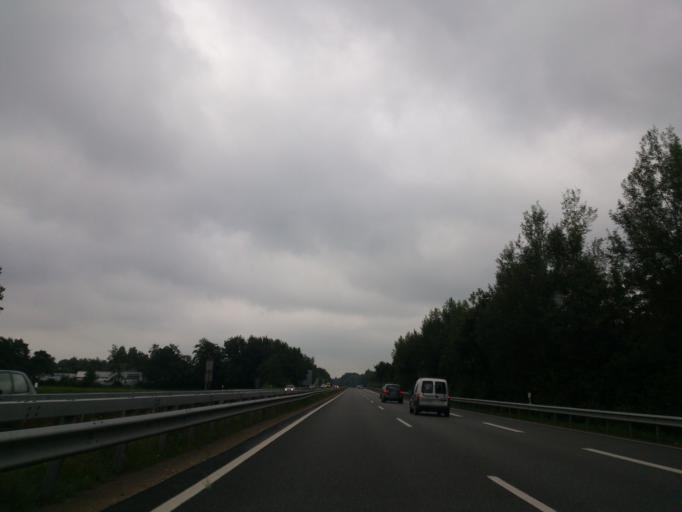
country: DE
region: Schleswig-Holstein
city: Ottenbuttel
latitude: 53.9567
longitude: 9.4902
